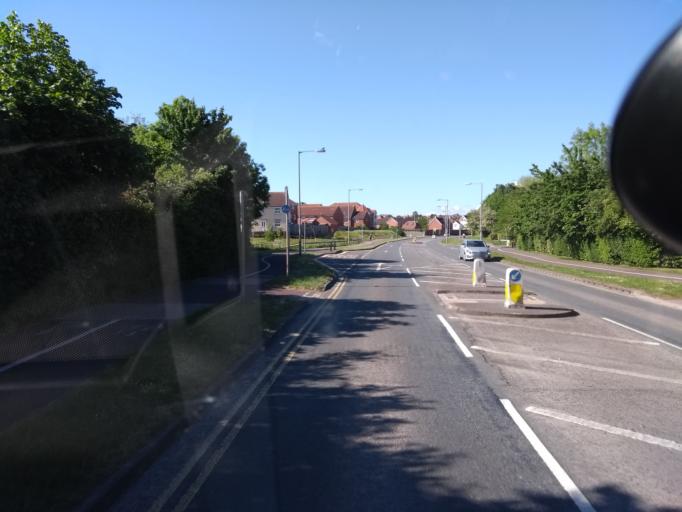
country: GB
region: England
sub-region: Somerset
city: Bridgwater
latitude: 51.1319
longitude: -3.0177
